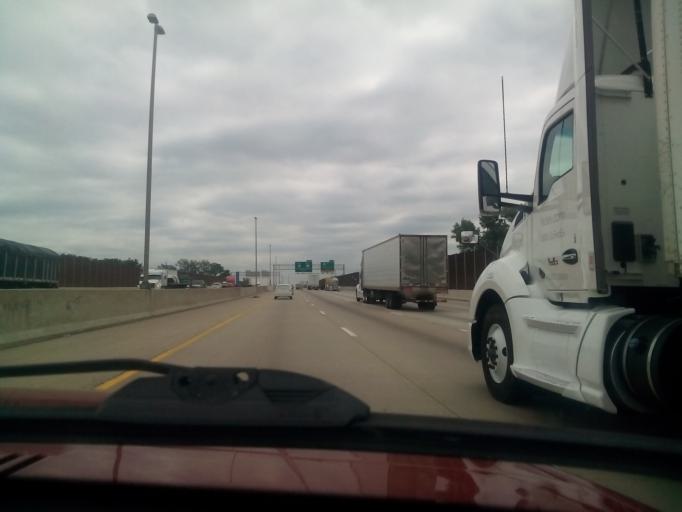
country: US
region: Indiana
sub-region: Lake County
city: Munster
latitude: 41.5769
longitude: -87.5250
